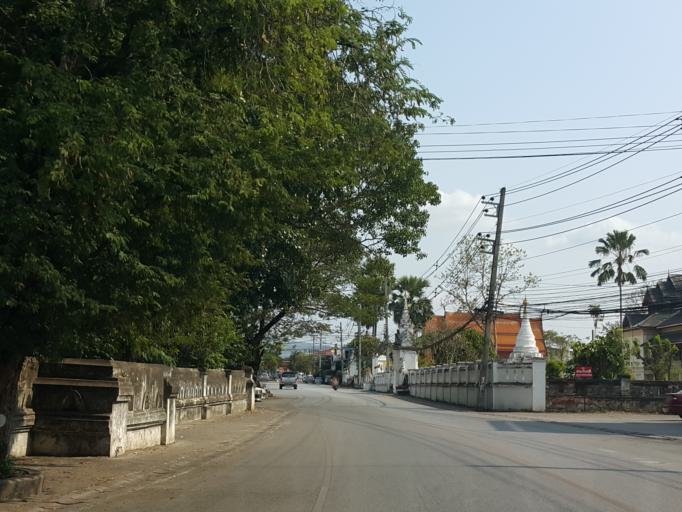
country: TH
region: Lampang
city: Lampang
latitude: 18.2844
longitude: 99.5048
